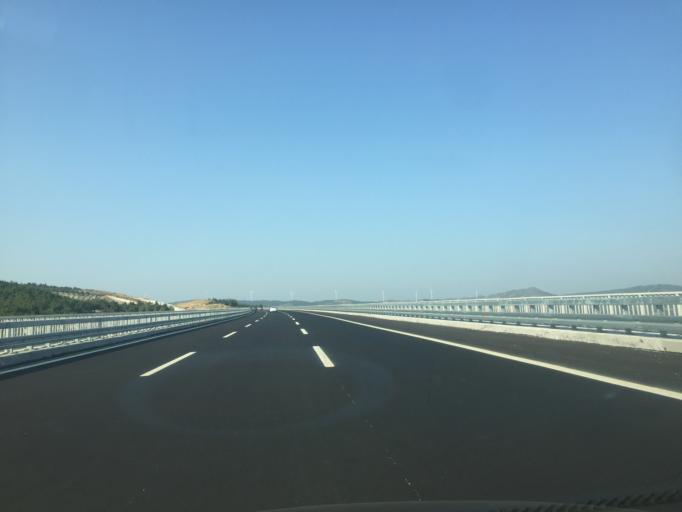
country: TR
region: Manisa
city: Zeytinliova
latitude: 39.0097
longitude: 27.7459
